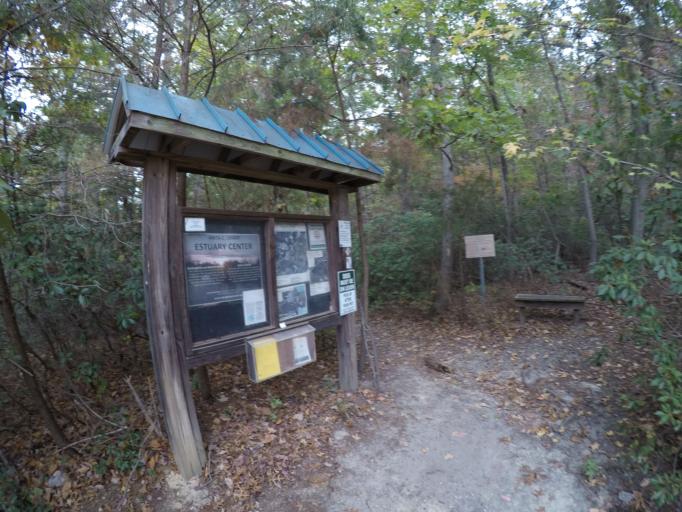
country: US
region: Maryland
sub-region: Harford County
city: Riverside
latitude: 39.4502
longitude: -76.2686
